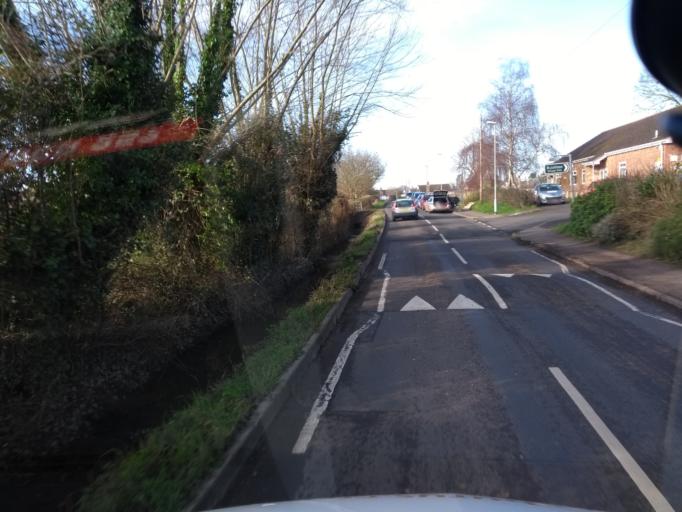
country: GB
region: England
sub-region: Somerset
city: Creech Saint Michael
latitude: 51.0195
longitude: -3.0443
